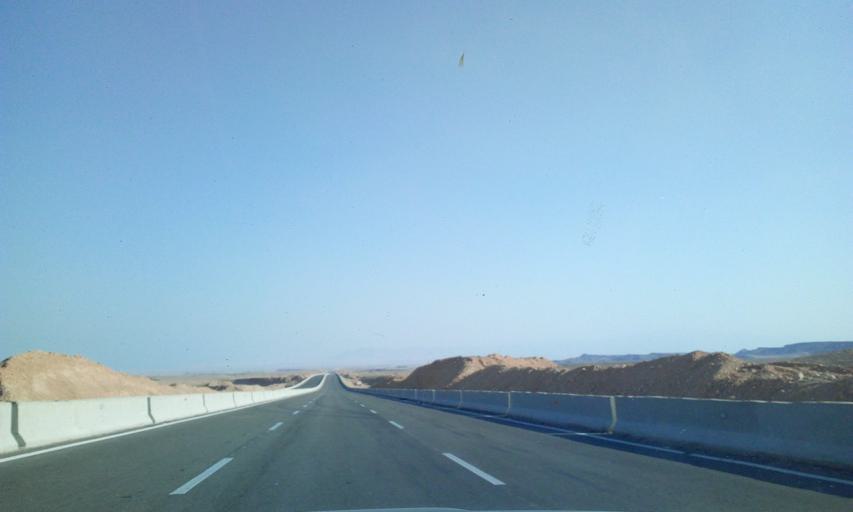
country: EG
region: As Suways
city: Ain Sukhna
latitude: 29.2556
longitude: 32.4763
